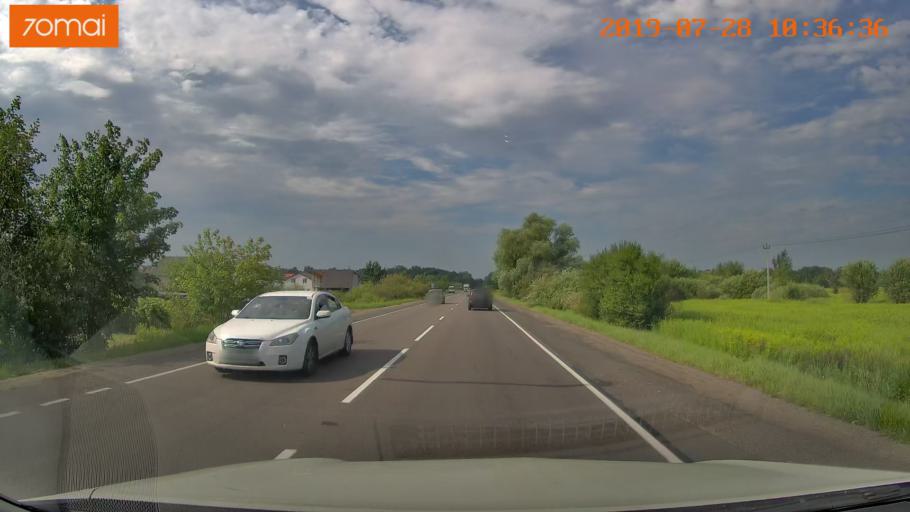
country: RU
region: Kaliningrad
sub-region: Gorod Kaliningrad
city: Kaliningrad
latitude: 54.7370
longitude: 20.4196
